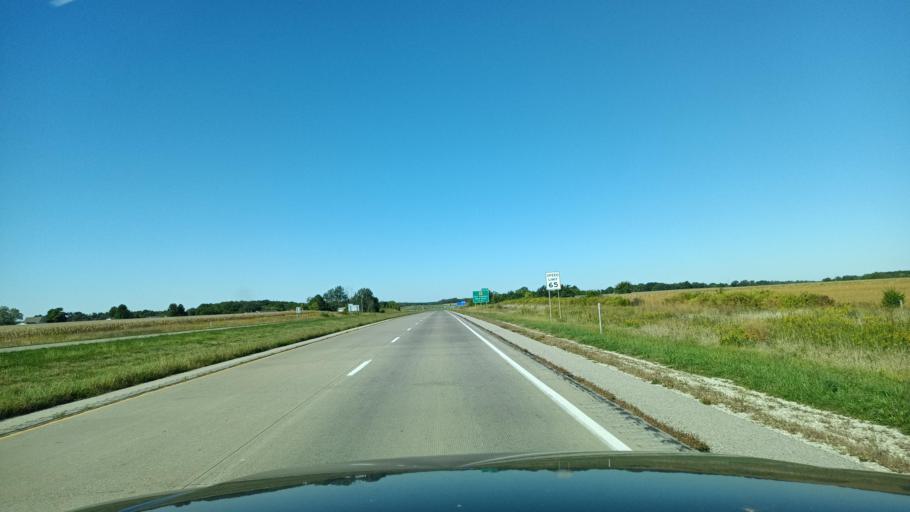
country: US
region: Iowa
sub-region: Lee County
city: Fort Madison
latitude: 40.6706
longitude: -91.3382
